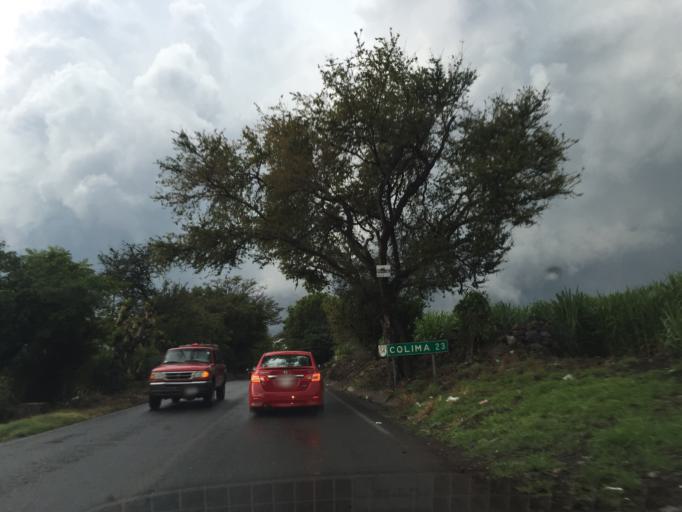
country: MX
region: Colima
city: Queseria
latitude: 19.3809
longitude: -103.5744
